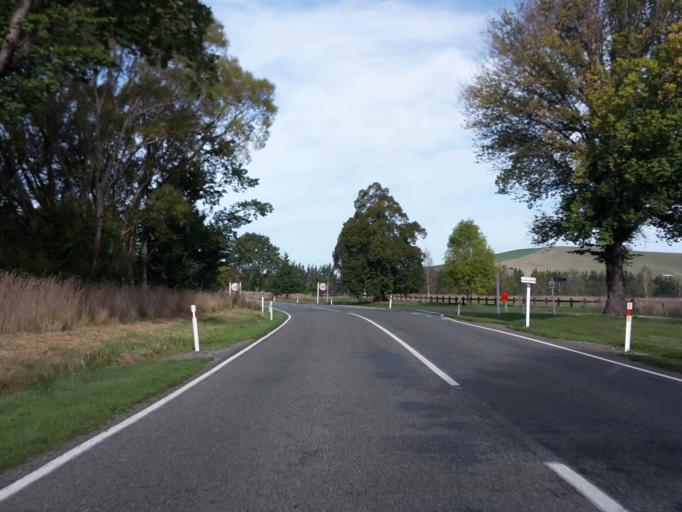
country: NZ
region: Canterbury
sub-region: Timaru District
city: Pleasant Point
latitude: -44.0465
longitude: 170.7587
